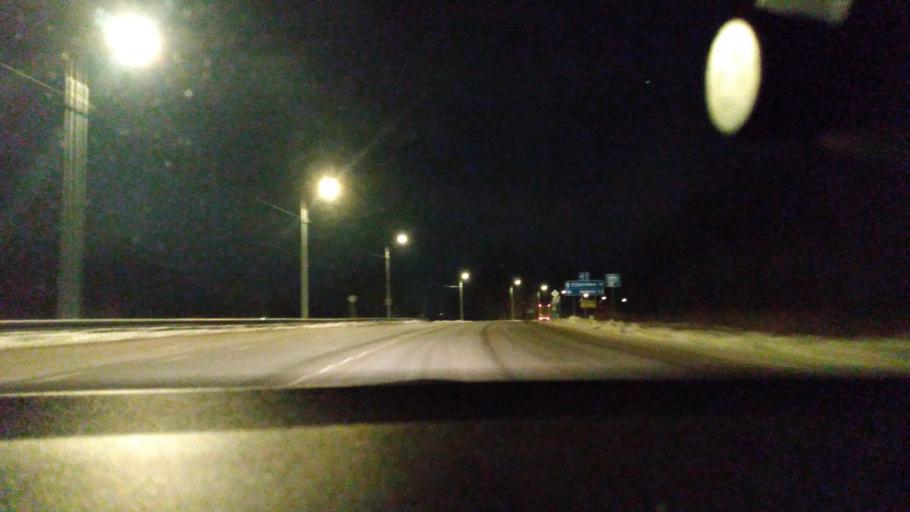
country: RU
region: Moskovskaya
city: Yegor'yevsk
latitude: 55.3094
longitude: 39.0785
